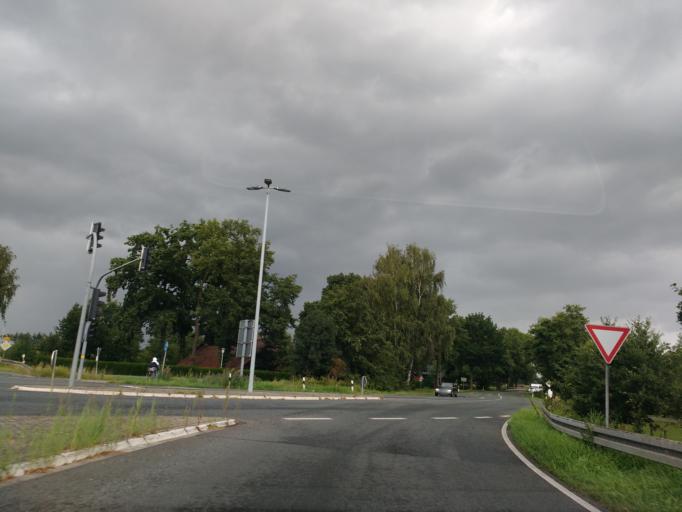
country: DE
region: Lower Saxony
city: Glandorf
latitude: 52.0830
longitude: 8.0083
